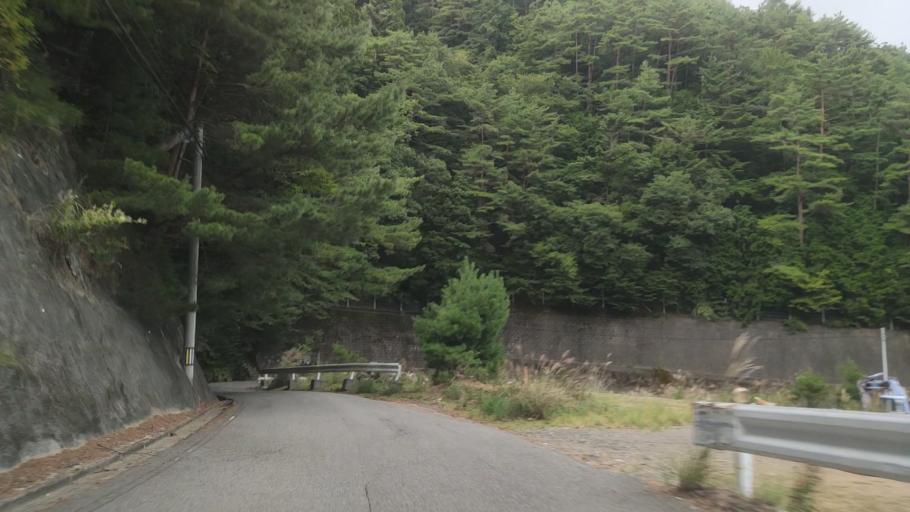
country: JP
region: Wakayama
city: Koya
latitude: 34.2234
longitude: 135.6148
